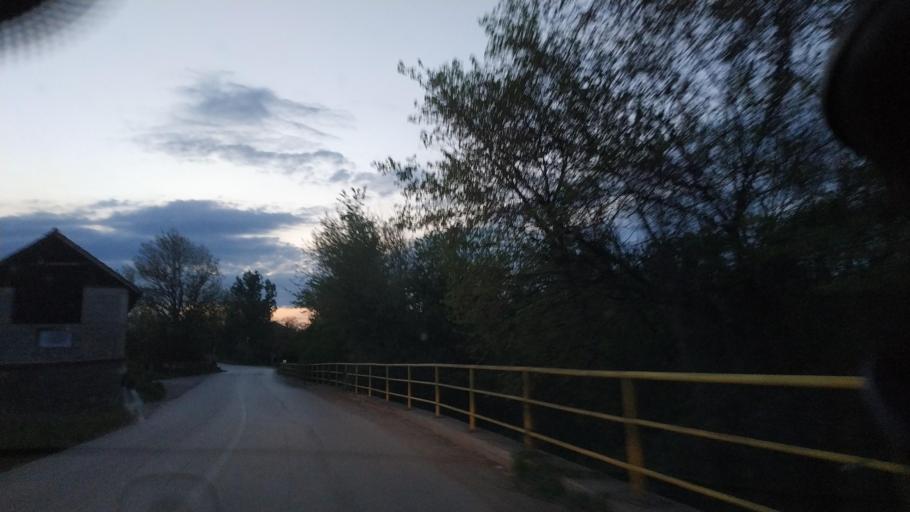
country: RS
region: Central Serbia
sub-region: Nisavski Okrug
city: Merosina
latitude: 43.2997
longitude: 21.6997
